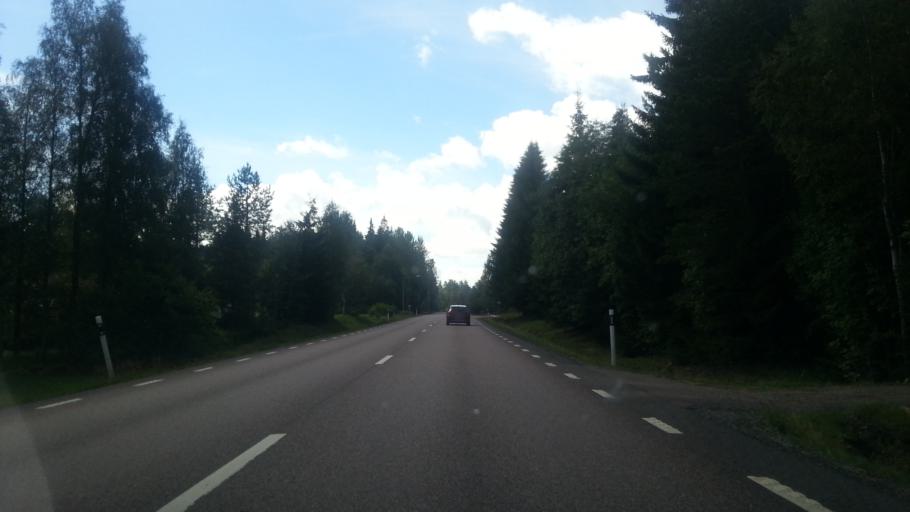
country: SE
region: Dalarna
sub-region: Ludvika Kommun
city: Ludvika
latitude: 60.2280
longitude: 15.2299
